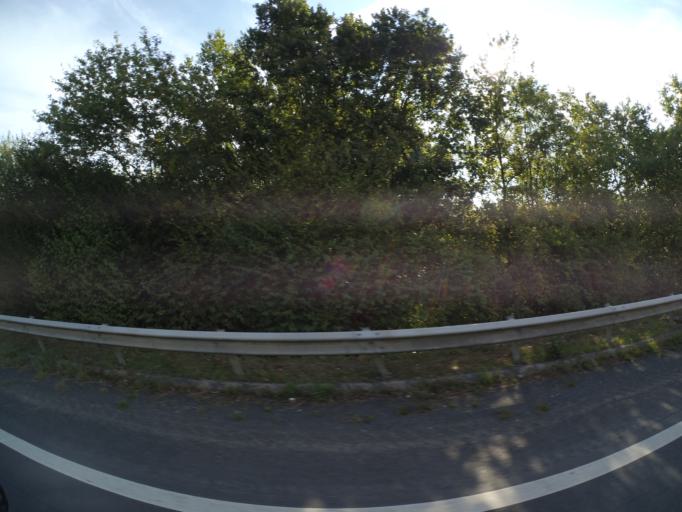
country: FR
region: Pays de la Loire
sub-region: Departement de la Loire-Atlantique
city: Clisson
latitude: 47.1078
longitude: -1.2810
